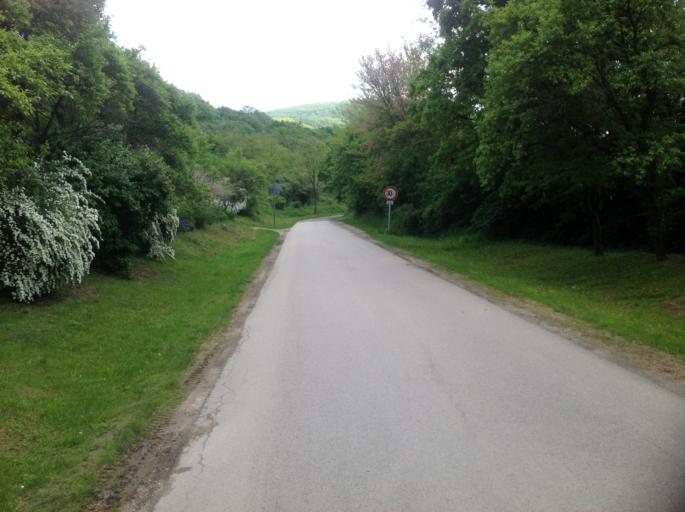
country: HU
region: Komarom-Esztergom
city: Kesztolc
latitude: 47.7137
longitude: 18.8122
